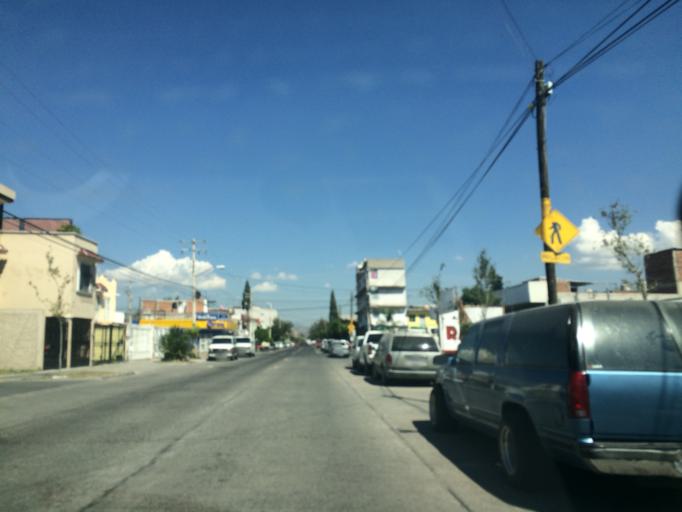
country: MX
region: Guanajuato
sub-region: Leon
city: San Jose de Duran (Los Troncoso)
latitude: 21.0910
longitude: -101.6519
